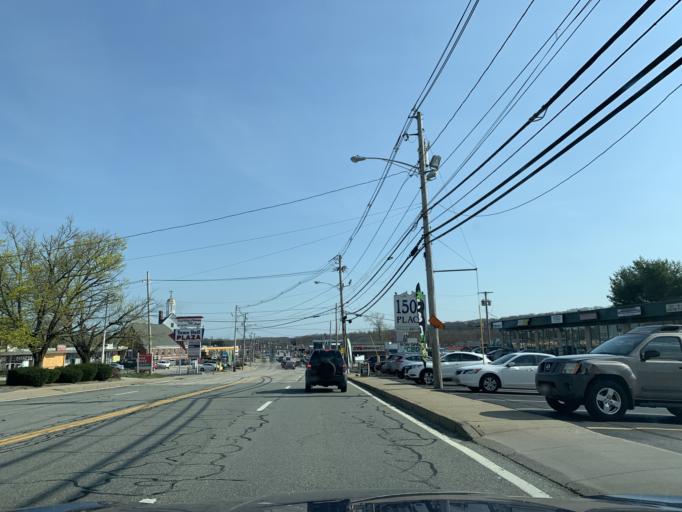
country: US
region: Rhode Island
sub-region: Providence County
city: Johnston
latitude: 41.8257
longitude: -71.4997
